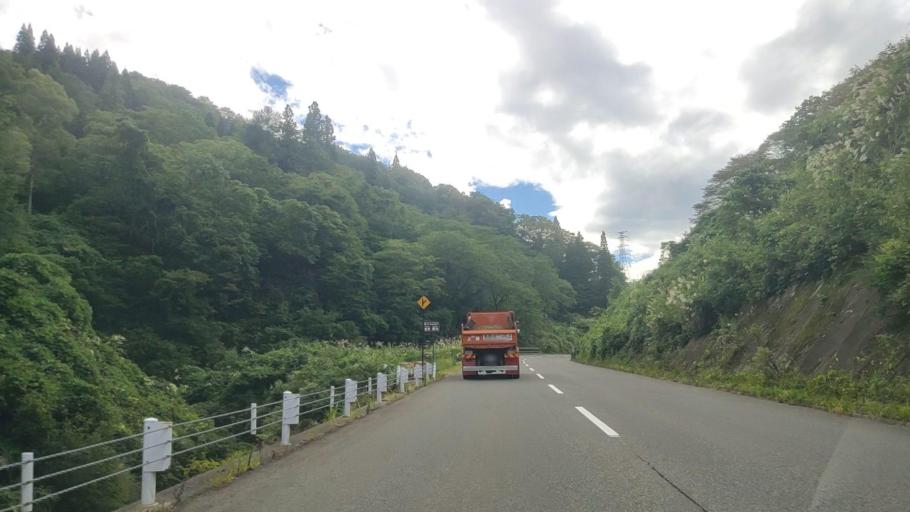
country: JP
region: Nagano
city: Iiyama
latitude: 36.8966
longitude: 138.3208
